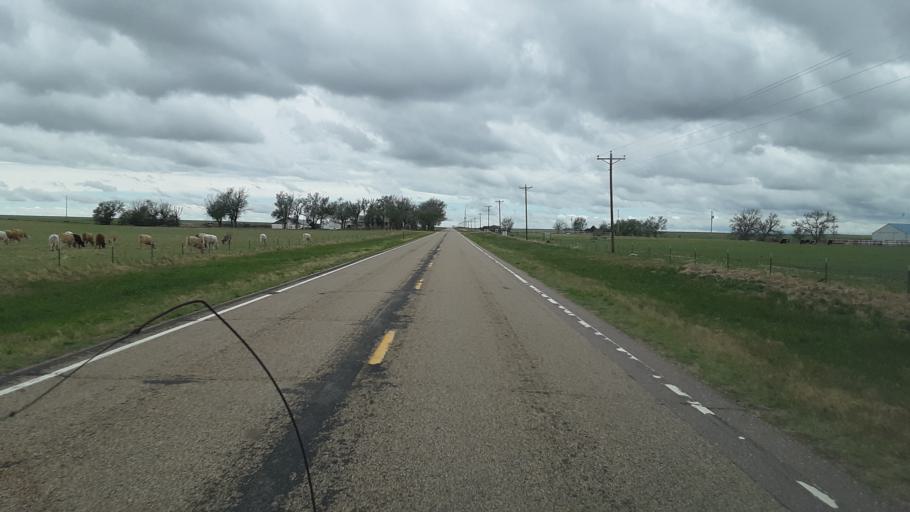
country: US
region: Colorado
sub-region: El Paso County
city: Ellicott
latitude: 38.8398
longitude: -103.9949
